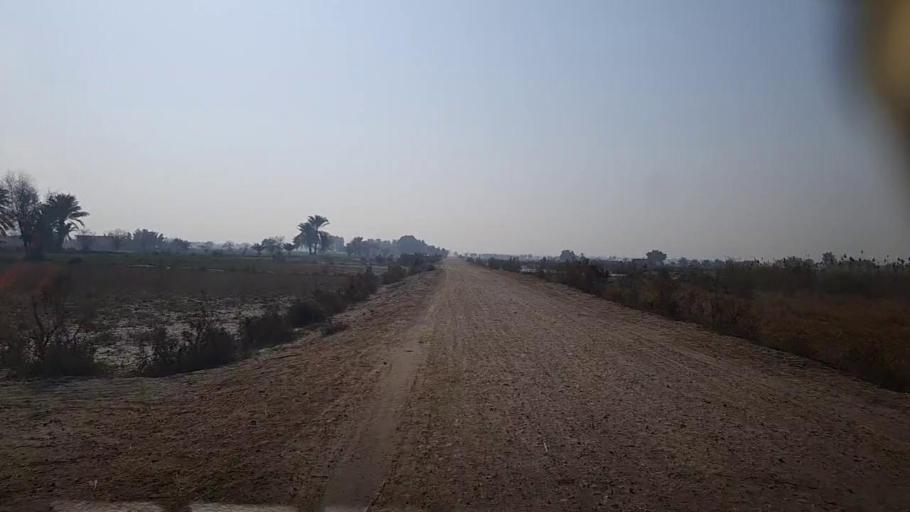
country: PK
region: Sindh
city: Karaundi
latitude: 26.8519
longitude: 68.3981
